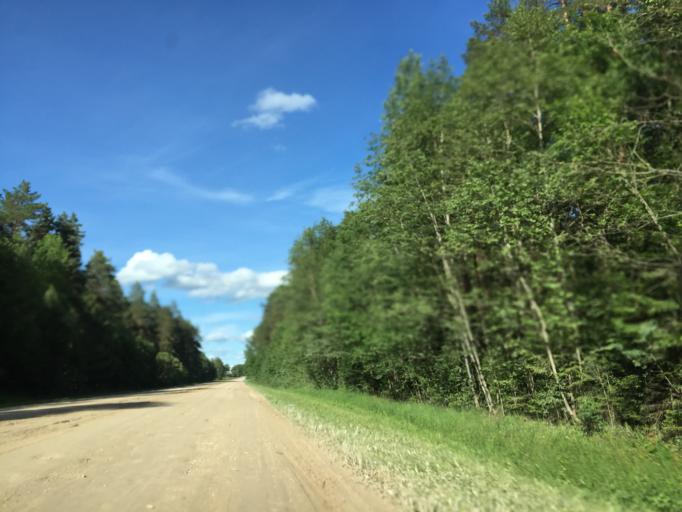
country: LV
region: Vecumnieki
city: Vecumnieki
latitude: 56.4470
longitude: 24.5830
